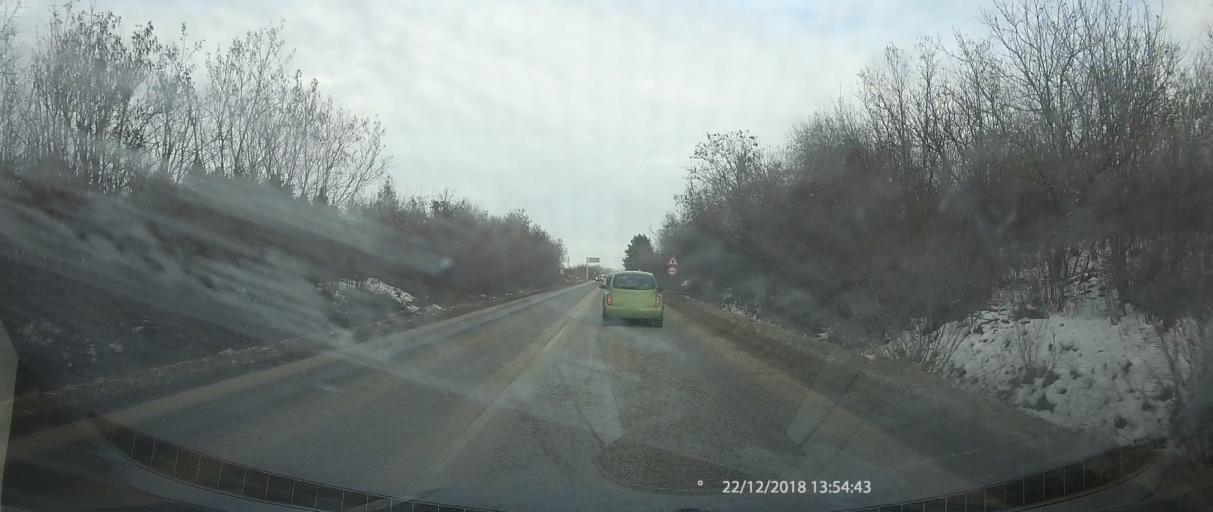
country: BG
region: Pleven
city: Iskur
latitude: 43.3251
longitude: 24.2709
